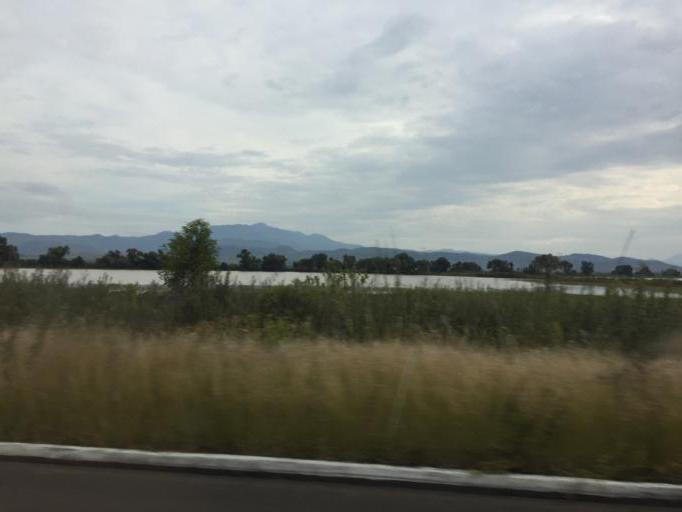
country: MX
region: Mexico
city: Huaniqueo de Morales
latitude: 19.8934
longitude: -101.5418
